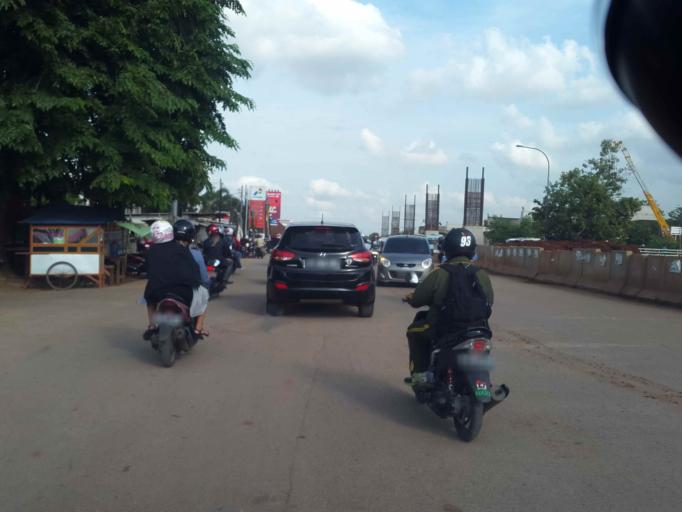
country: ID
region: West Java
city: Bekasi
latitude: -6.2481
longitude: 106.9289
